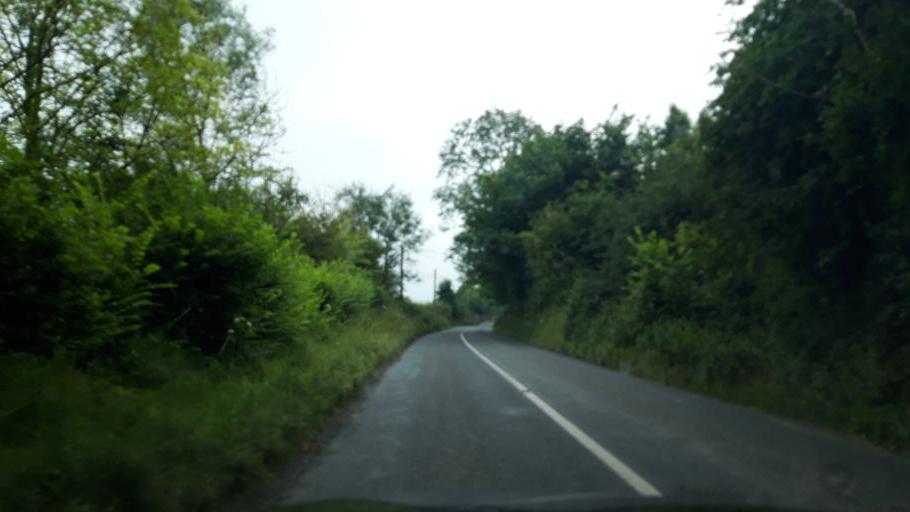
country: IE
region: Munster
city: Fethard
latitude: 52.5343
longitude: -7.6811
